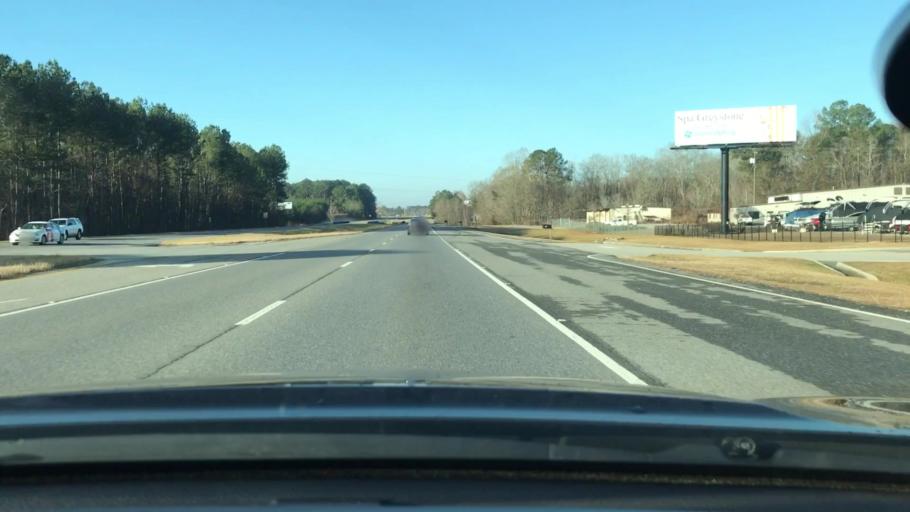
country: US
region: Alabama
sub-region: Shelby County
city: Westover
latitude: 33.3543
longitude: -86.5224
